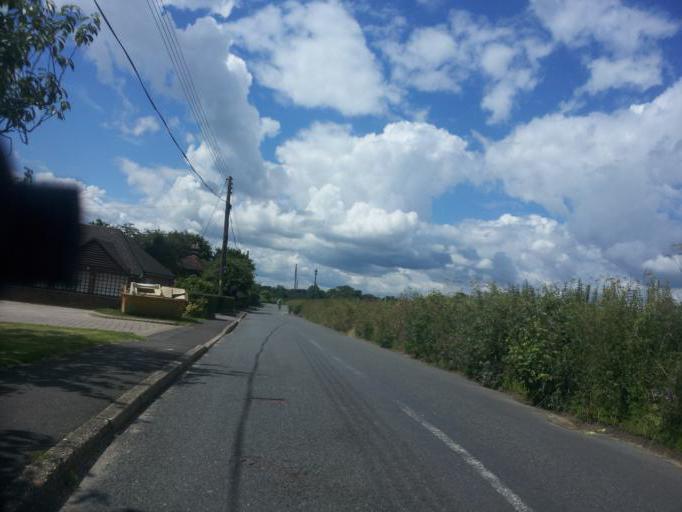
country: GB
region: England
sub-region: Kent
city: West Malling
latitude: 51.3163
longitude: 0.4032
